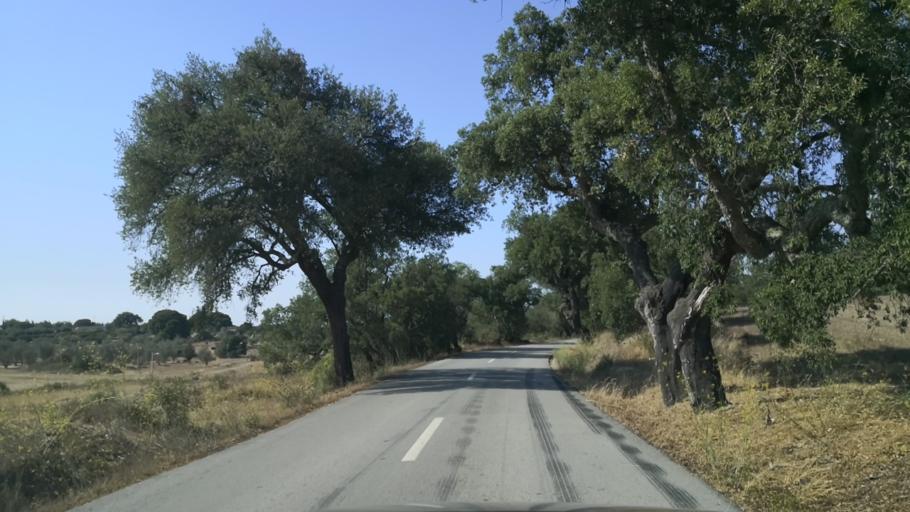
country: PT
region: Santarem
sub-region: Benavente
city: Poceirao
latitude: 38.7563
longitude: -8.6324
